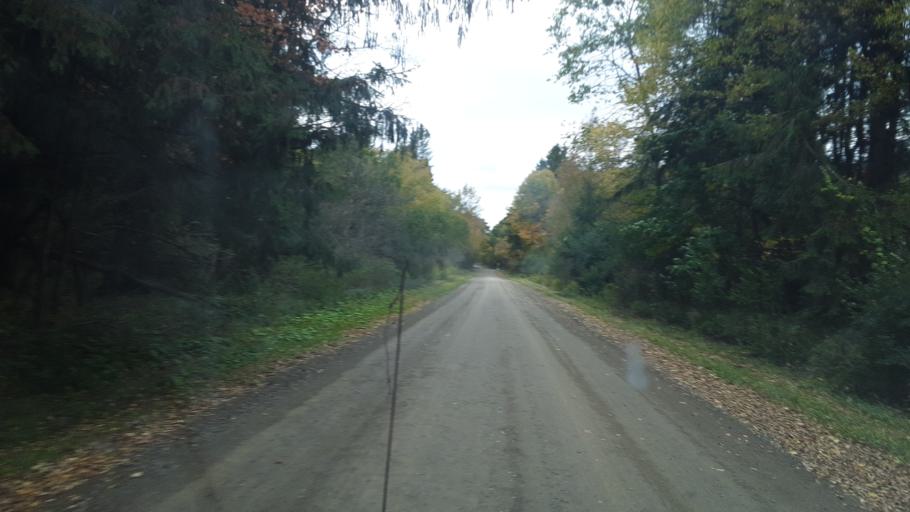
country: US
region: New York
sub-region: Allegany County
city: Alfred
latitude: 42.3702
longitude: -77.8488
